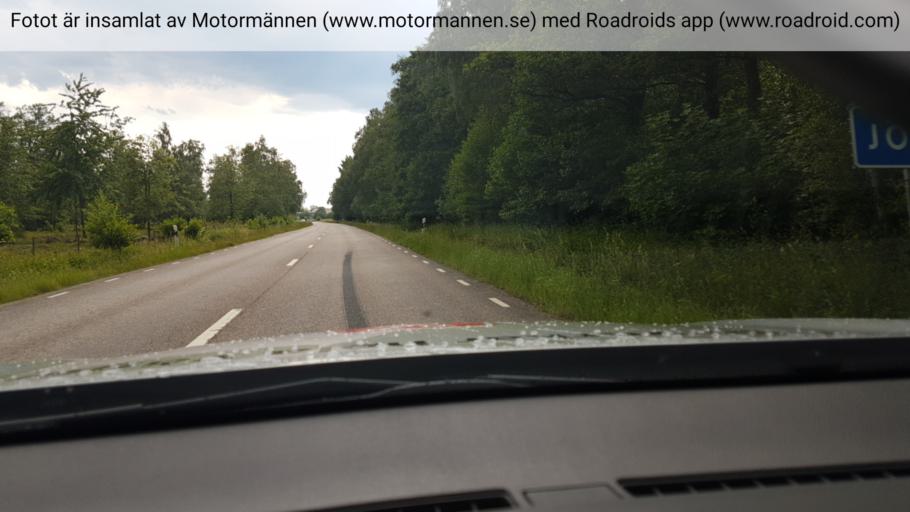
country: SE
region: Vaestra Goetaland
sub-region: Hjo Kommun
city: Hjo
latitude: 58.2228
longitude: 14.2083
